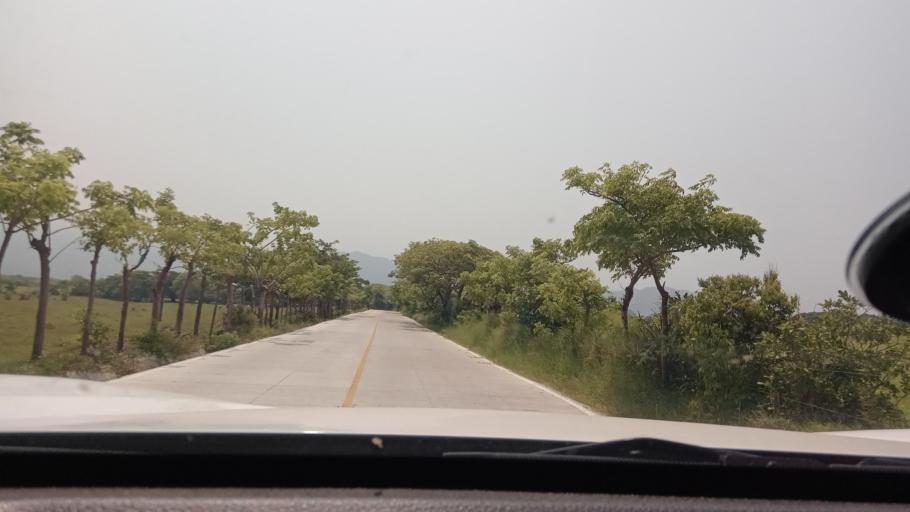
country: MX
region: Veracruz
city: Catemaco
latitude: 18.5596
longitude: -95.0228
